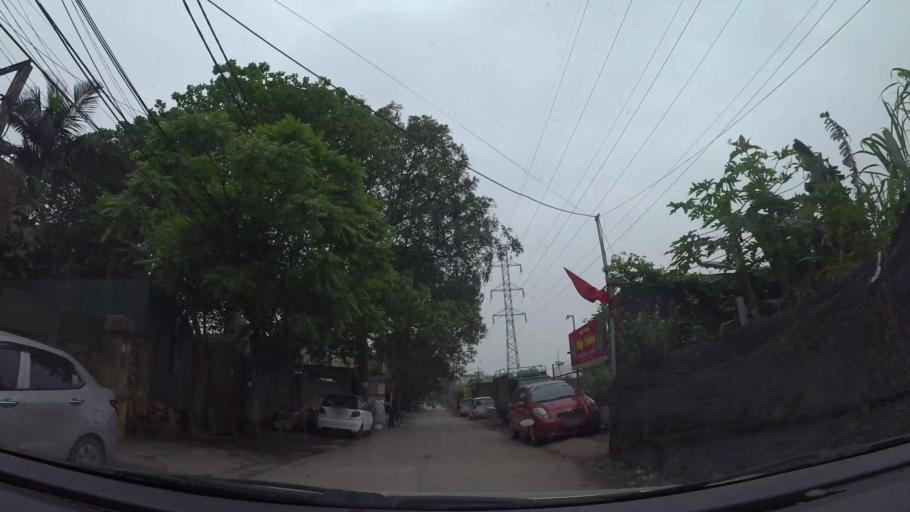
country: VN
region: Ha Noi
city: Tay Ho
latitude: 21.0586
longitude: 105.8400
